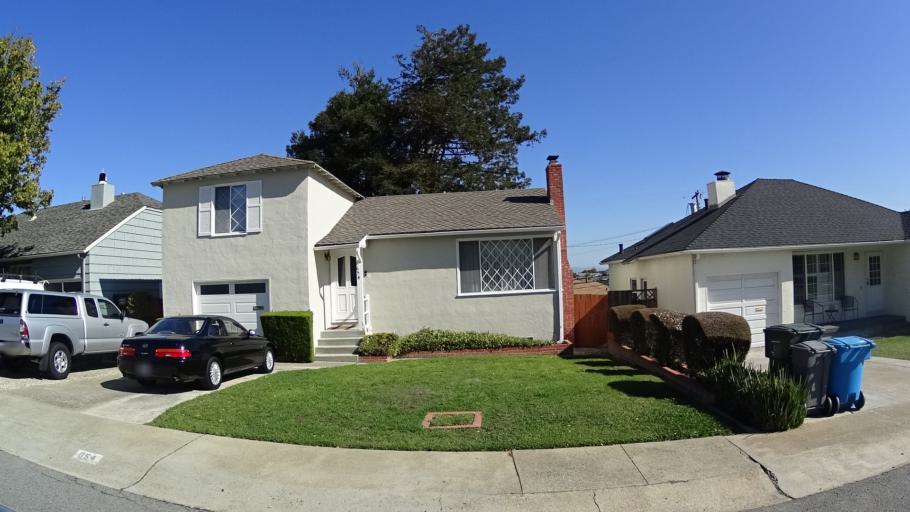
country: US
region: California
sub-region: San Mateo County
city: San Bruno
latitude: 37.6230
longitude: -122.4227
